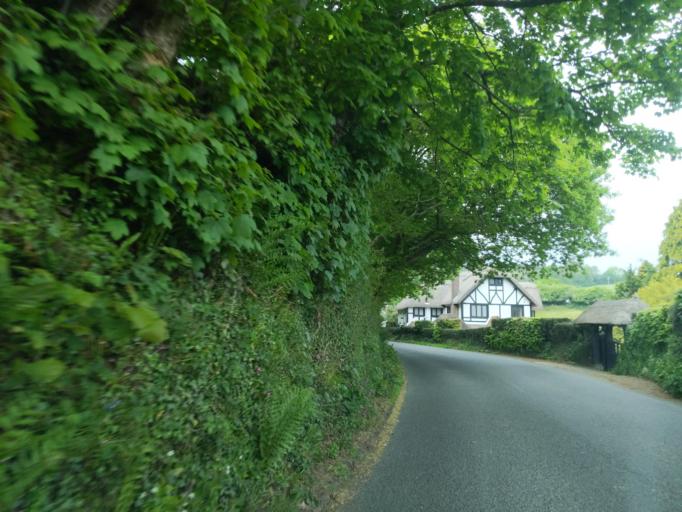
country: GB
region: England
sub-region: Devon
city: Plympton
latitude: 50.4103
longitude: -4.0521
